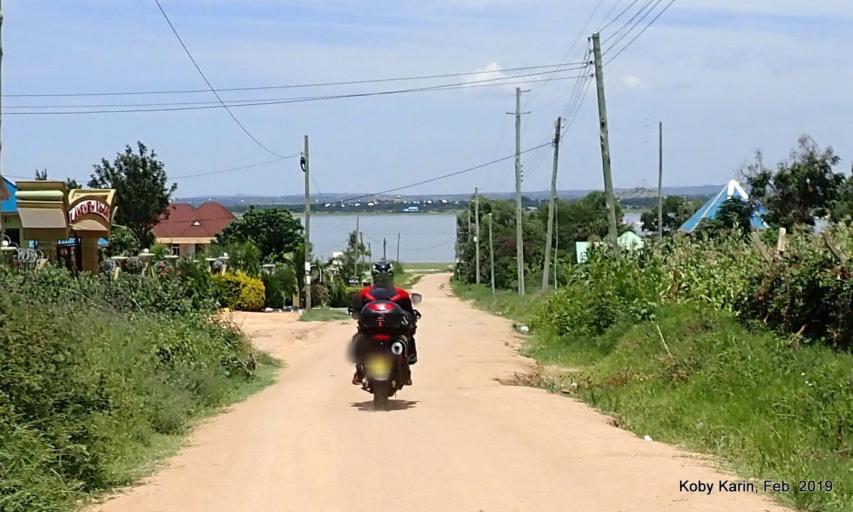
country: TZ
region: Singida
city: Singida
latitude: -4.7976
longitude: 34.7379
